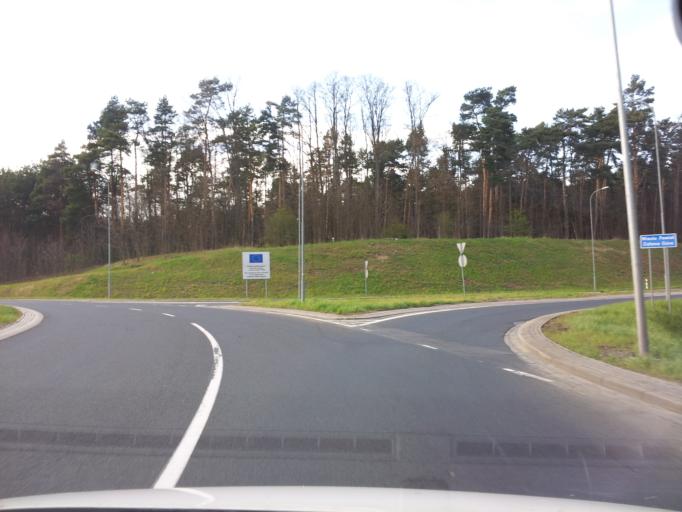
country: PL
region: Lubusz
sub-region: Zielona Gora
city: Zielona Gora
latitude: 51.9468
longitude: 15.4402
